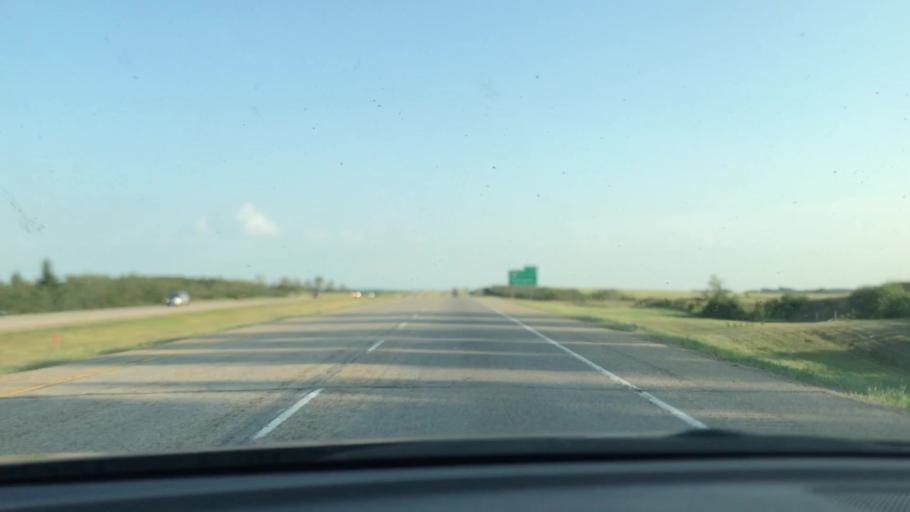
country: CA
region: Alberta
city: Ponoka
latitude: 52.5913
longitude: -113.6633
